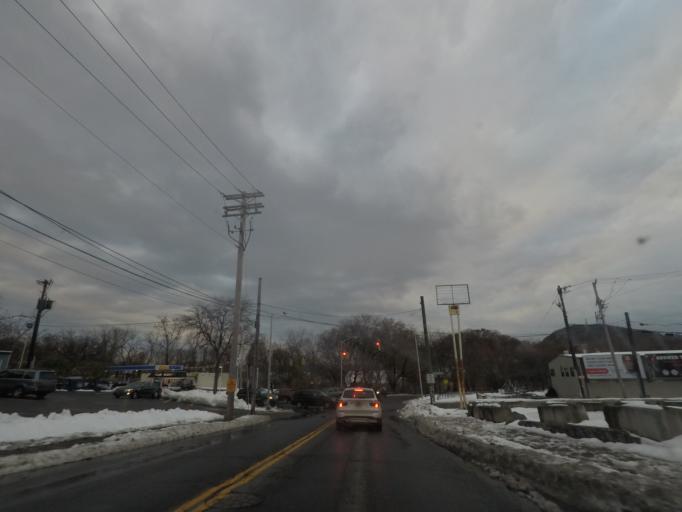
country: US
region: New York
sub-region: Orange County
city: Newburgh
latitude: 41.5012
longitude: -74.0309
